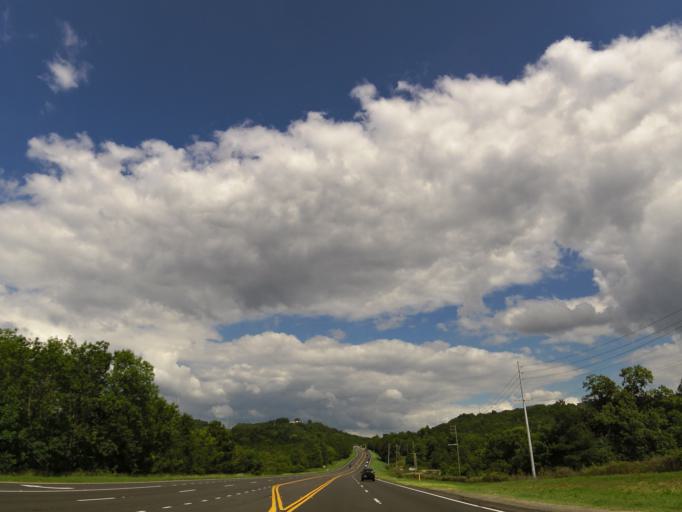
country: US
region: Georgia
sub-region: Walker County
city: Fairview
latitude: 34.9509
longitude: -85.3110
